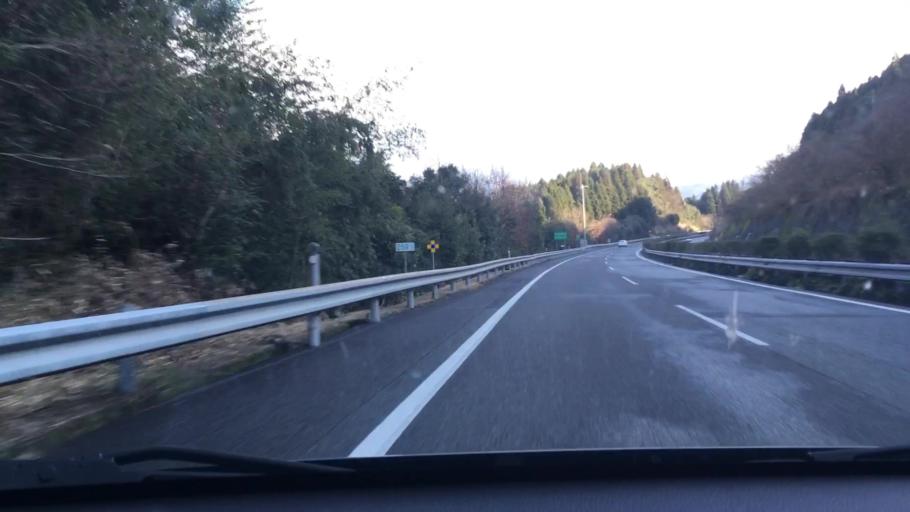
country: JP
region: Kumamoto
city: Hitoyoshi
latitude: 32.1787
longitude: 130.7868
